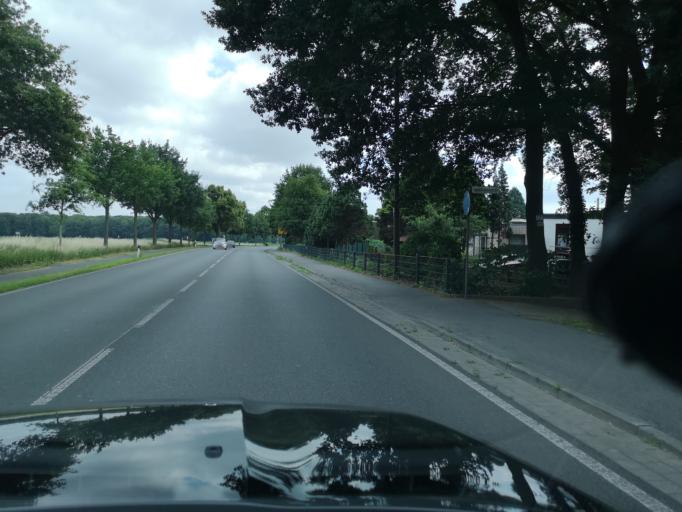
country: DE
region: North Rhine-Westphalia
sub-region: Regierungsbezirk Dusseldorf
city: Wesel
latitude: 51.6734
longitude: 6.6413
